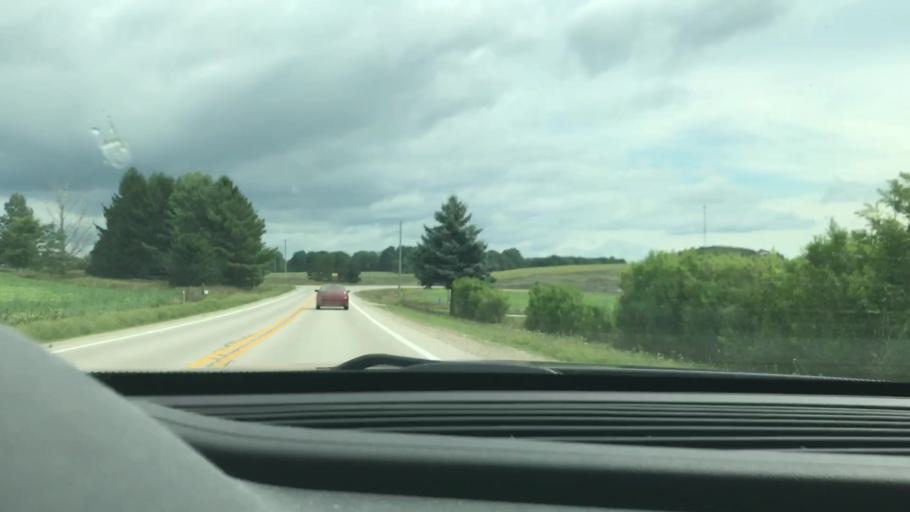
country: US
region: Michigan
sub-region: Antrim County
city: Bellaire
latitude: 45.0936
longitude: -85.2923
